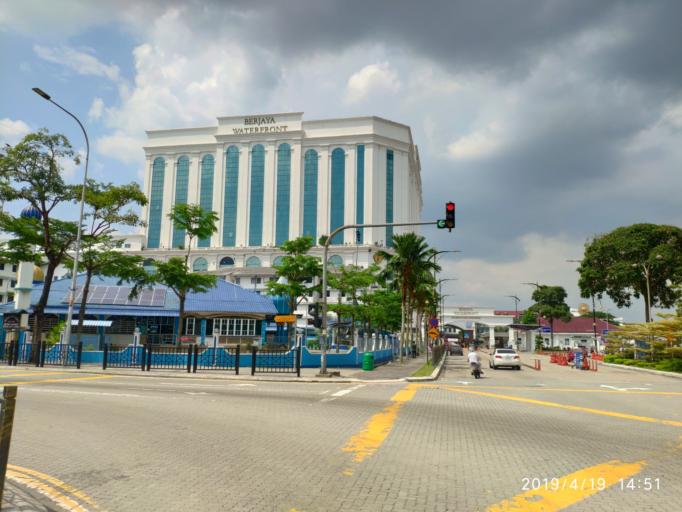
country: MY
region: Johor
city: Johor Bahru
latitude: 1.4698
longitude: 103.7820
